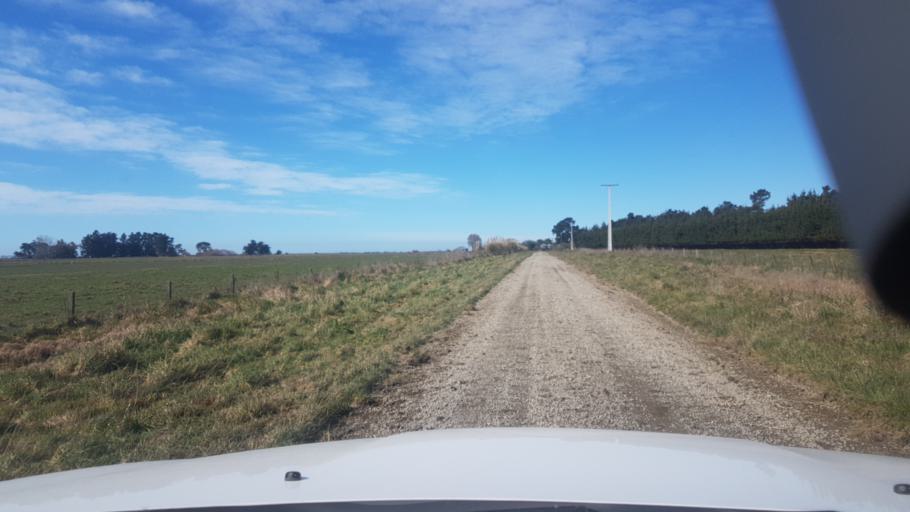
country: NZ
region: Canterbury
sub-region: Timaru District
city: Timaru
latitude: -44.2642
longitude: 171.3503
